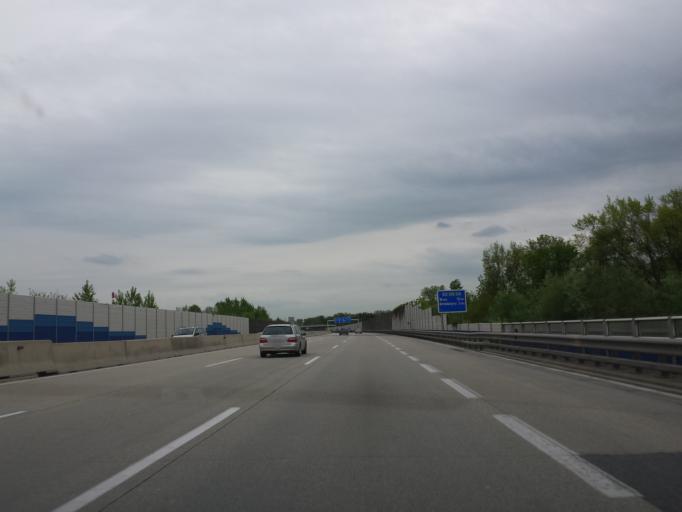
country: AT
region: Lower Austria
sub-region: Politischer Bezirk Korneuburg
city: Korneuburg
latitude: 48.3461
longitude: 16.3204
